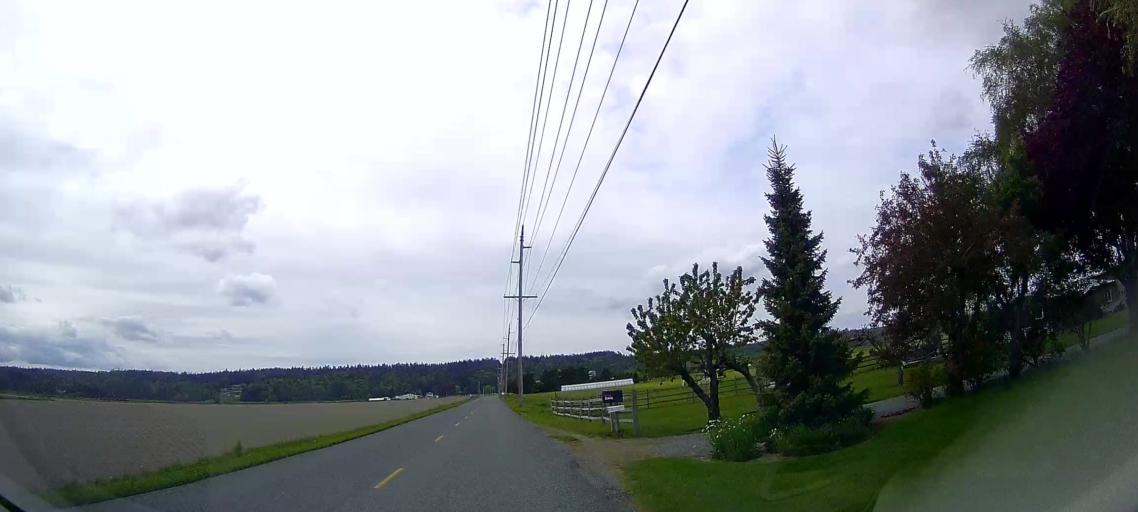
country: US
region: Washington
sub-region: Skagit County
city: Mount Vernon
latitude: 48.4210
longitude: -122.4827
